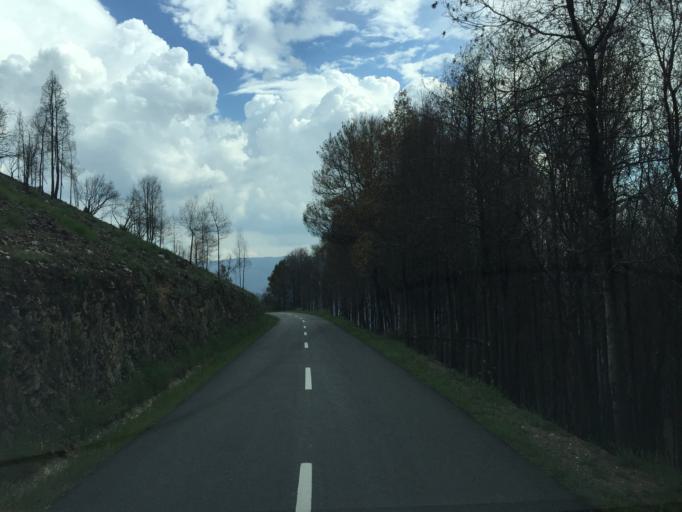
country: PT
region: Coimbra
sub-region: Arganil
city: Arganil
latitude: 40.1782
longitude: -7.9748
